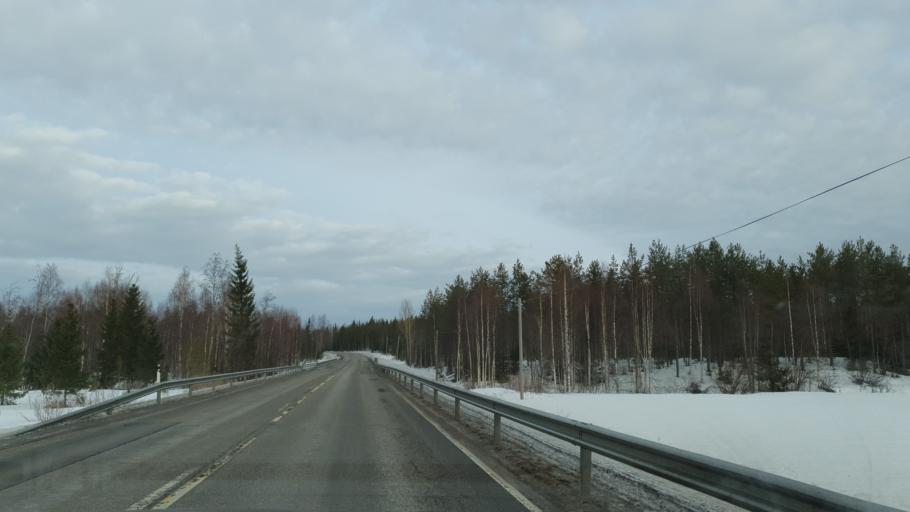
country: FI
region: Kainuu
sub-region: Kajaani
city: Vuokatti
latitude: 64.1960
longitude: 28.1713
